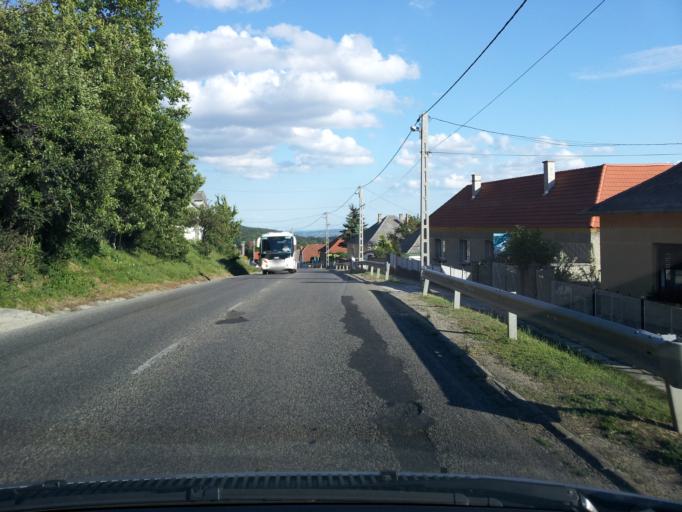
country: HU
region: Veszprem
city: Zirc
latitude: 47.2145
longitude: 17.9093
